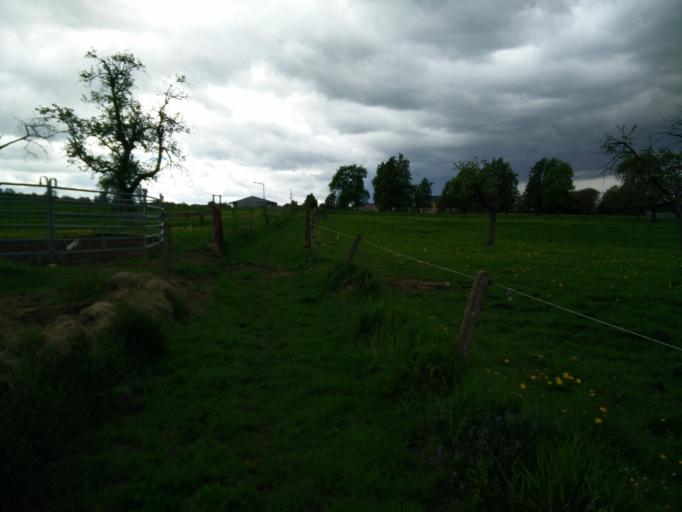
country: BE
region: Flanders
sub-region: Provincie Limburg
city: Sint-Pieters-Voeren
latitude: 50.7332
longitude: 5.7754
